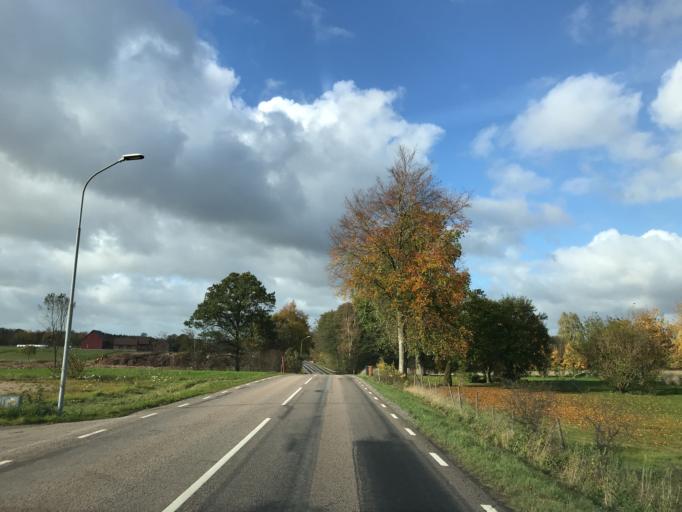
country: SE
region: Skane
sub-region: Svalovs Kommun
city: Kagerod
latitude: 56.0088
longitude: 13.0756
